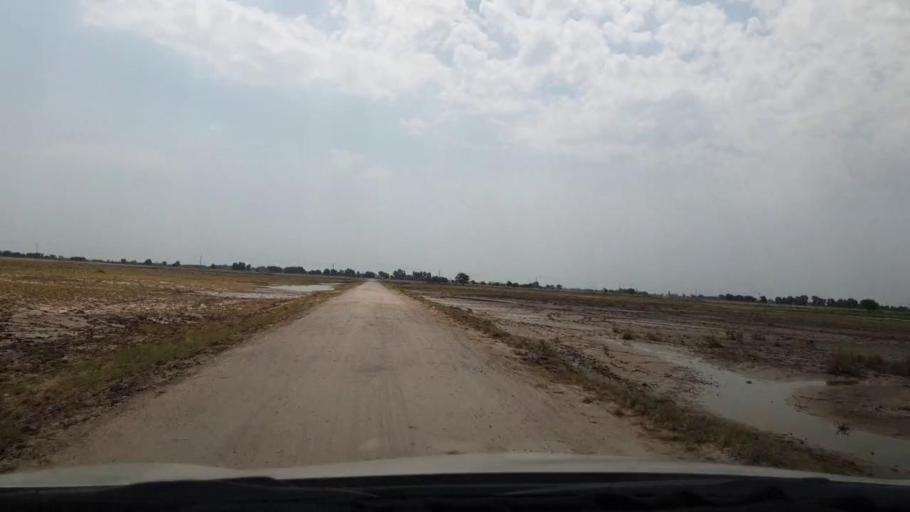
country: PK
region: Sindh
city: Ratodero
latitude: 27.8369
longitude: 68.3020
